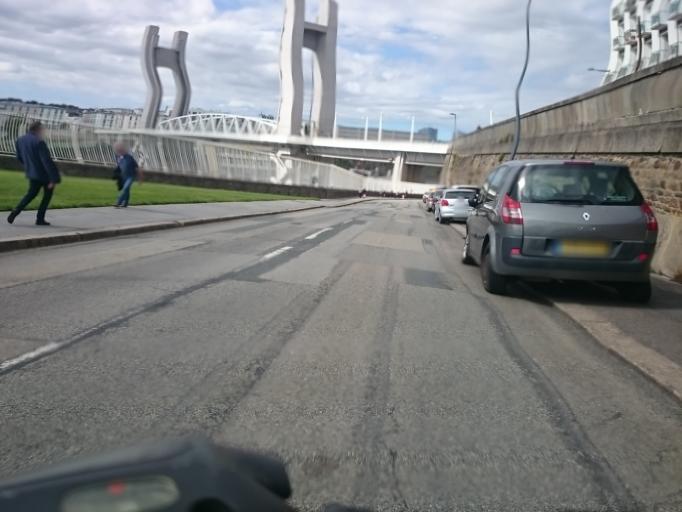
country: FR
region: Brittany
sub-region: Departement du Finistere
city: Brest
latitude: 48.3836
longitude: -4.4936
